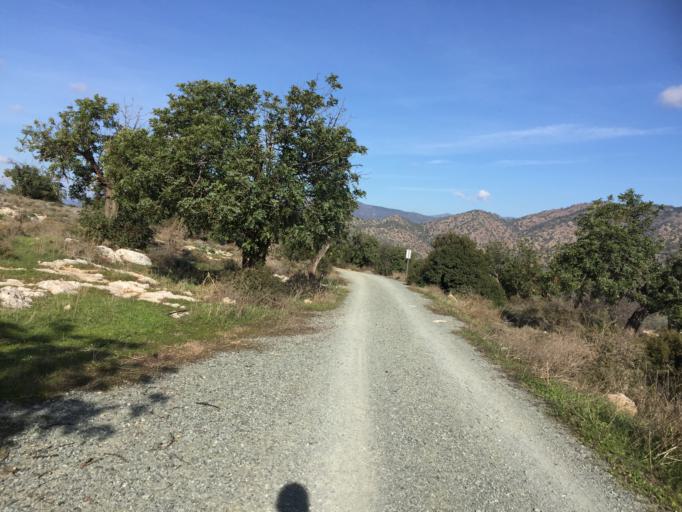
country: CY
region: Larnaka
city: Agios Tychon
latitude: 34.7465
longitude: 33.1273
